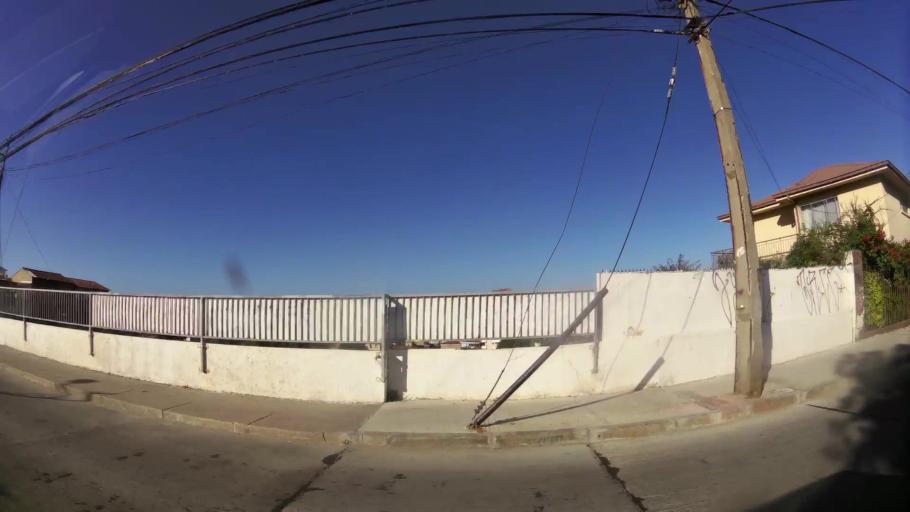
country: CL
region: Valparaiso
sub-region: Provincia de Valparaiso
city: Vina del Mar
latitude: -33.0273
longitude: -71.5659
